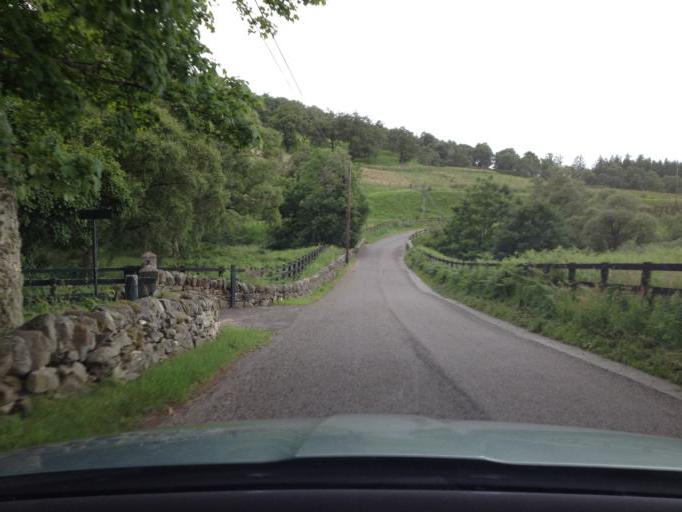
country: GB
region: Scotland
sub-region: Angus
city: Brechin
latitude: 56.8600
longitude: -2.6838
